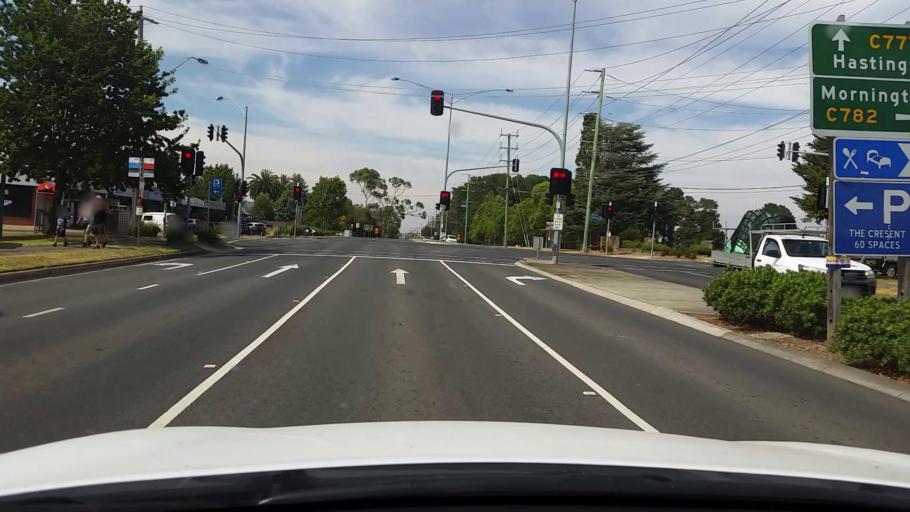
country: AU
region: Victoria
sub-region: Mornington Peninsula
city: Tyabb
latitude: -38.2609
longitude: 145.1898
